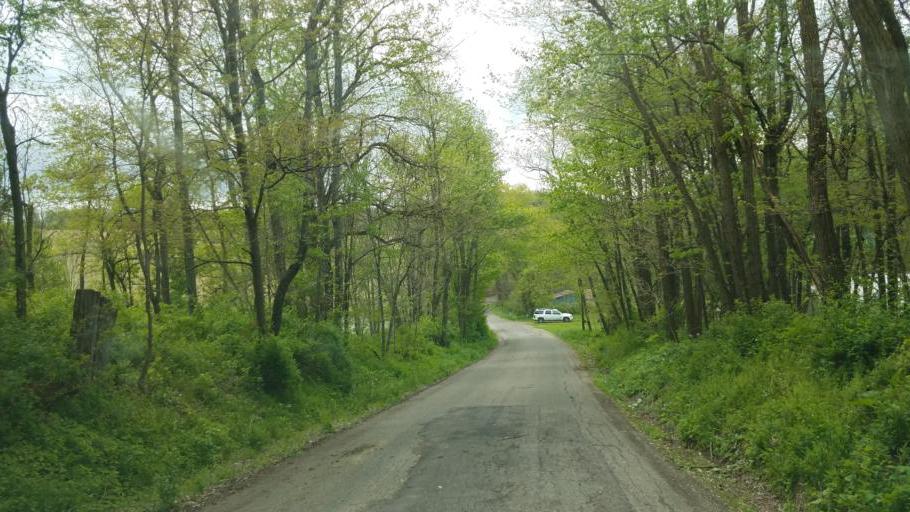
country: US
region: Ohio
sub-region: Sandusky County
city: Bellville
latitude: 40.5685
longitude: -82.3809
